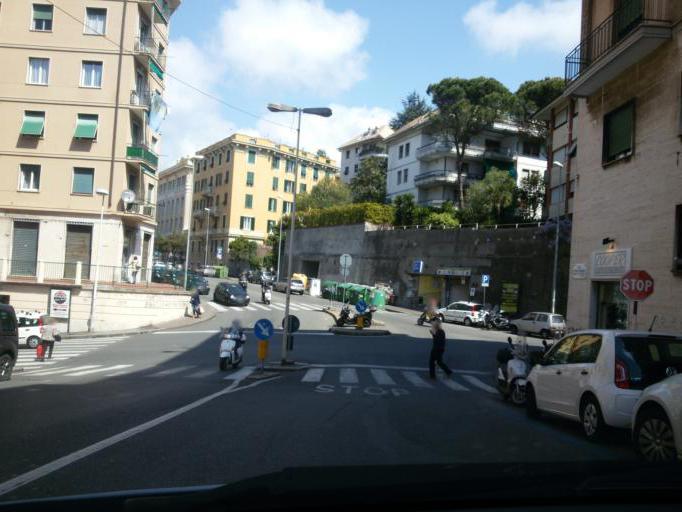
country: IT
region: Liguria
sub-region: Provincia di Genova
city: Genoa
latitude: 44.3983
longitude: 8.9646
